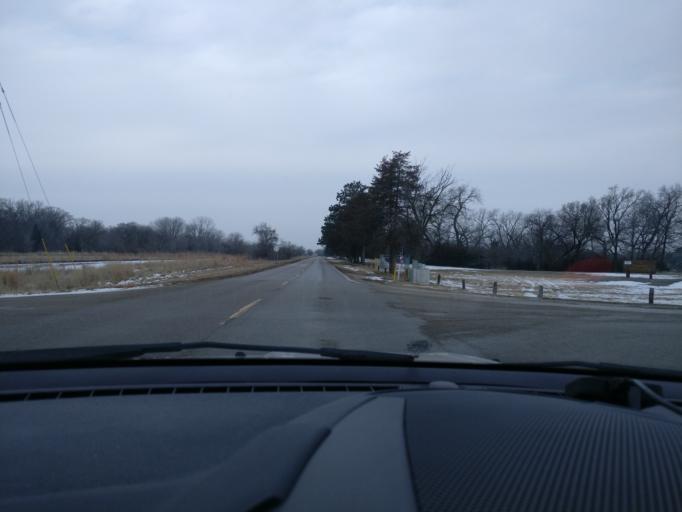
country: US
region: Nebraska
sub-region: Dodge County
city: Fremont
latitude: 41.4478
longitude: -96.5586
